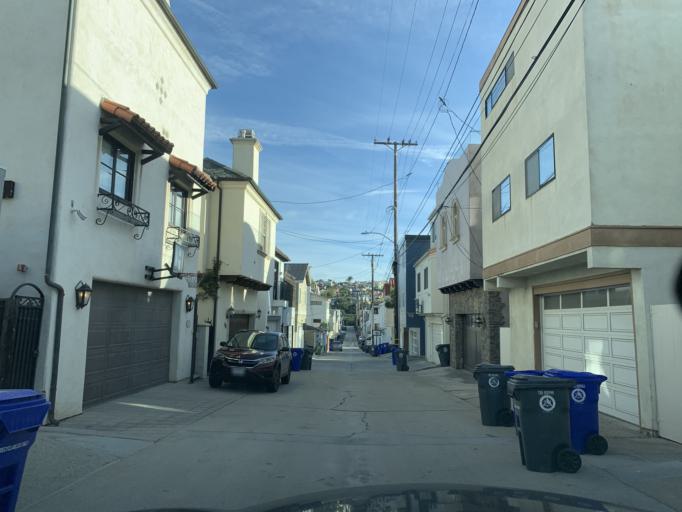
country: US
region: California
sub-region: Los Angeles County
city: Manhattan Beach
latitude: 33.8800
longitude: -118.4060
